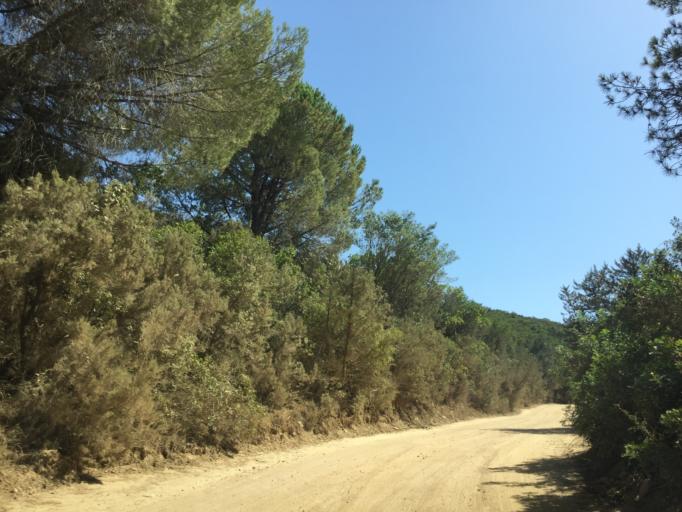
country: IT
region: Sardinia
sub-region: Provincia di Olbia-Tempio
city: San Teodoro
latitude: 40.8408
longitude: 9.7122
